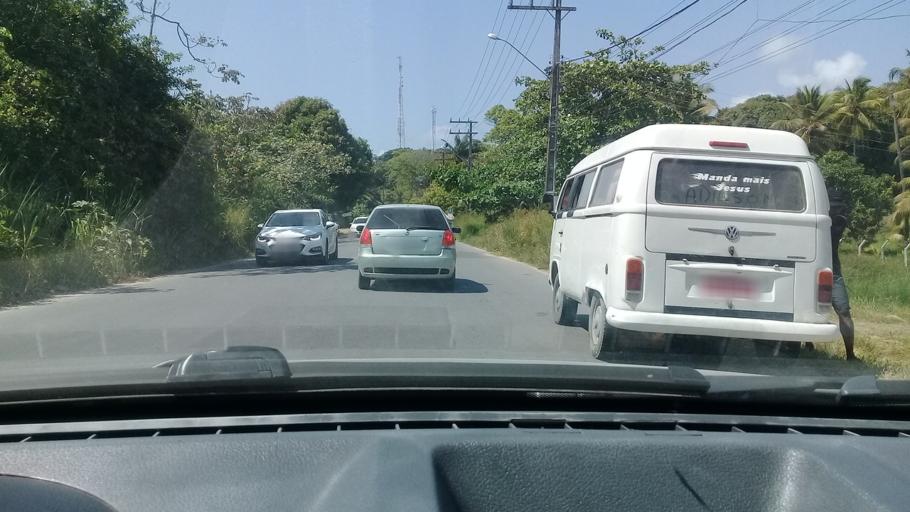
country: BR
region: Pernambuco
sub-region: Itamaraca
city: Itamaraca
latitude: -7.7722
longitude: -34.8363
